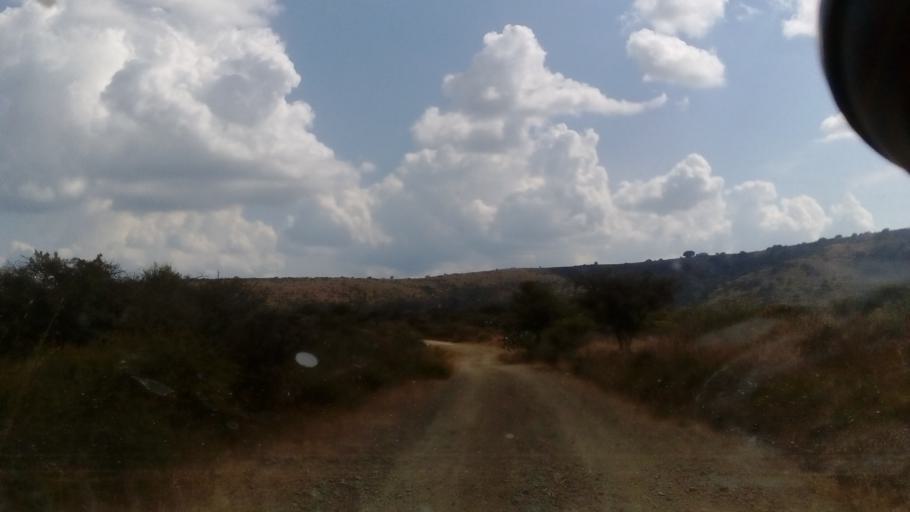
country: MX
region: Guanajuato
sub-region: Leon
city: Lucio Blanco (Los Gavilanes)
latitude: 21.1871
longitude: -101.4654
